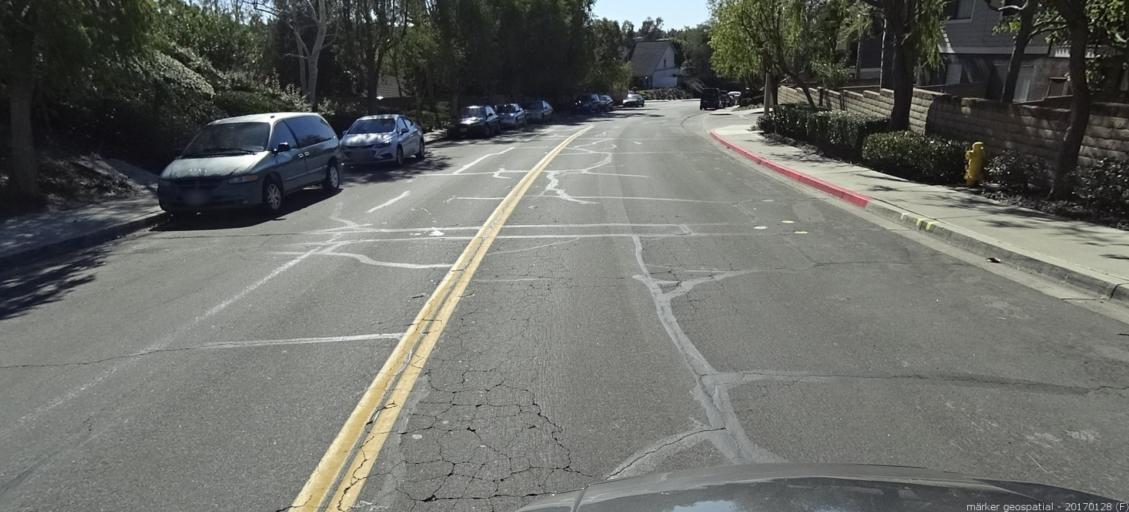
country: US
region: California
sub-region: Orange County
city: Lake Forest
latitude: 33.6545
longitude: -117.6848
